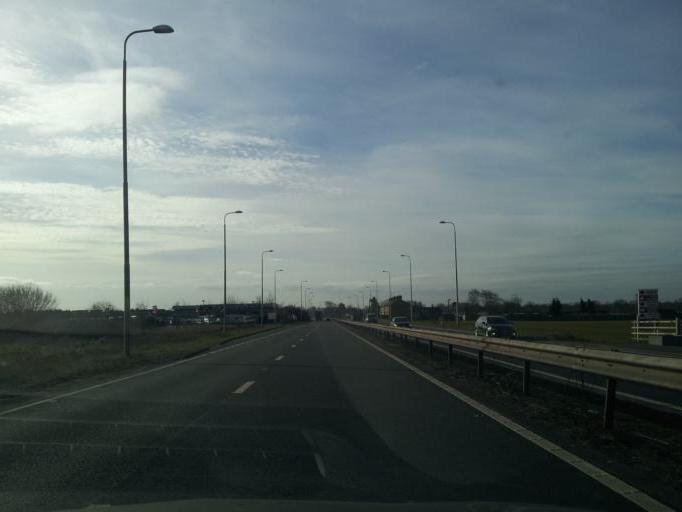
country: GB
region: England
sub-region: Central Bedfordshire
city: Blunham
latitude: 52.1472
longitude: -0.3012
